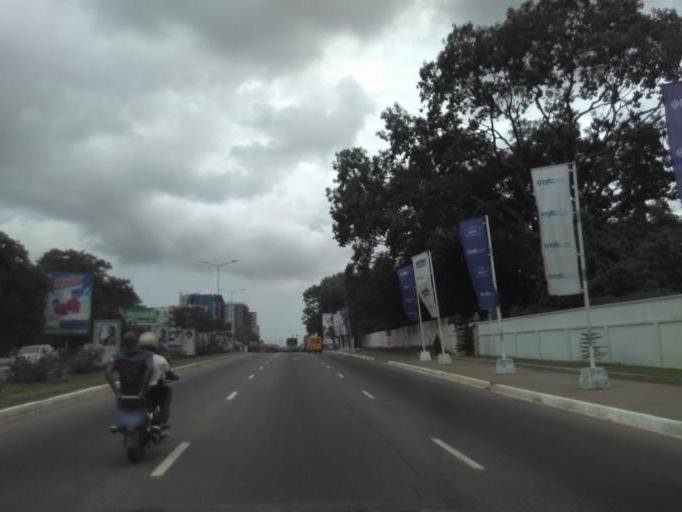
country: GH
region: Greater Accra
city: Accra
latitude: 5.6074
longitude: -0.1773
